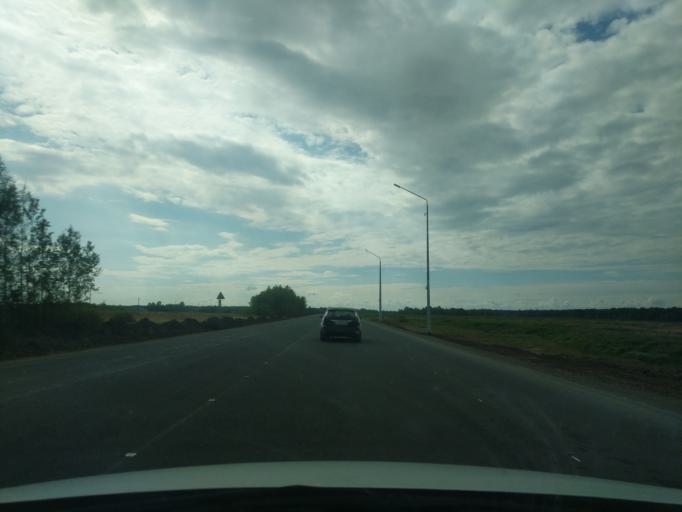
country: RU
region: Kostroma
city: Sudislavl'
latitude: 57.8330
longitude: 41.5489
